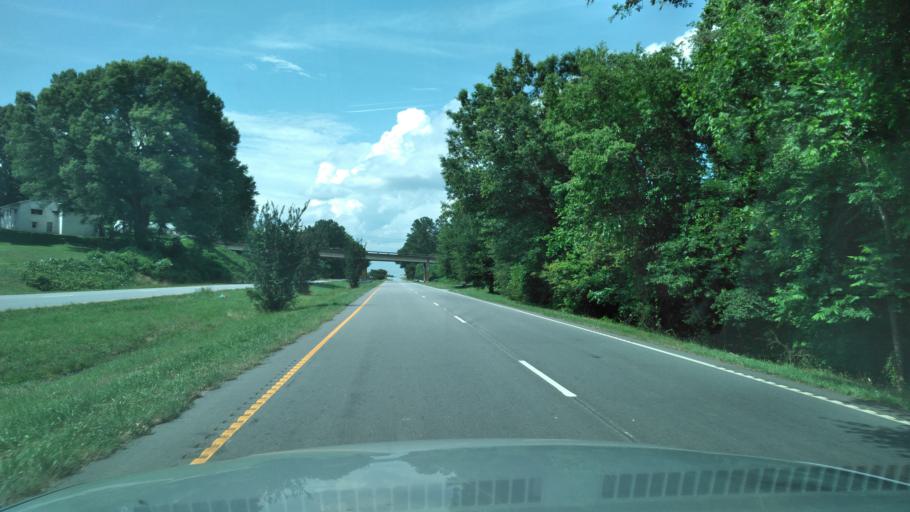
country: US
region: South Carolina
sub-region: Spartanburg County
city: Roebuck
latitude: 34.8656
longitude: -81.9609
